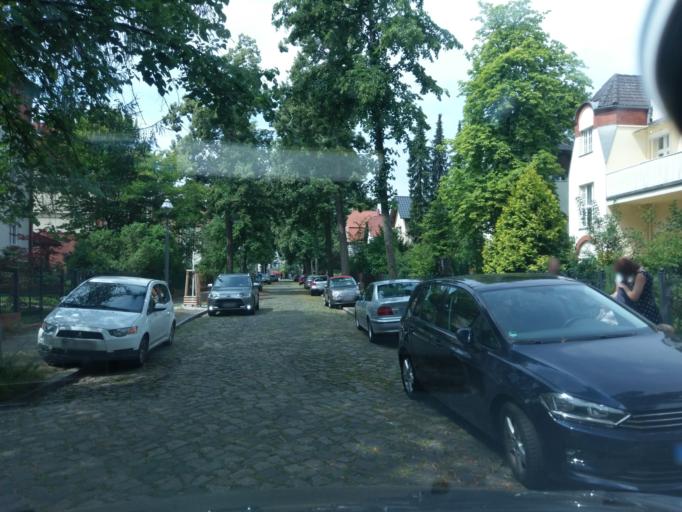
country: DE
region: Berlin
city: Lichterfelde
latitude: 52.4338
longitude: 13.2893
